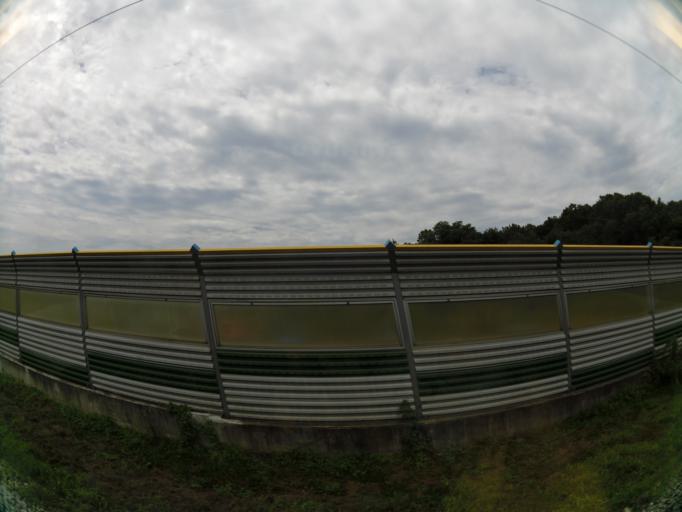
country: KR
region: Chungcheongnam-do
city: Cheonan
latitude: 36.7428
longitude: 127.1406
